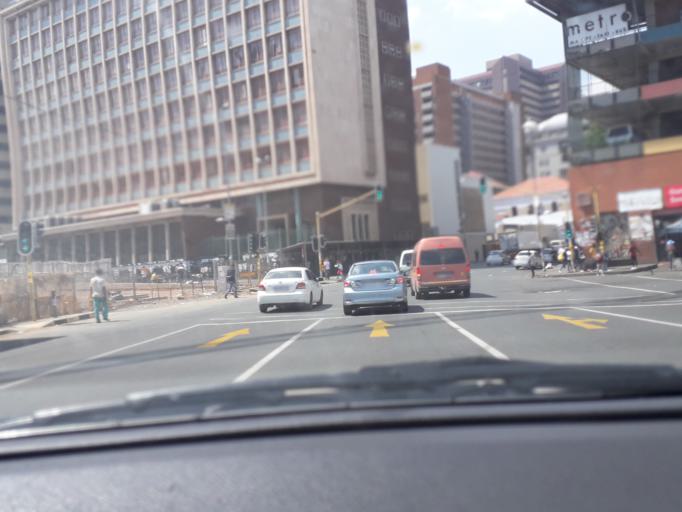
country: ZA
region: Gauteng
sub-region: City of Johannesburg Metropolitan Municipality
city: Johannesburg
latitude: -26.1998
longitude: 28.0386
